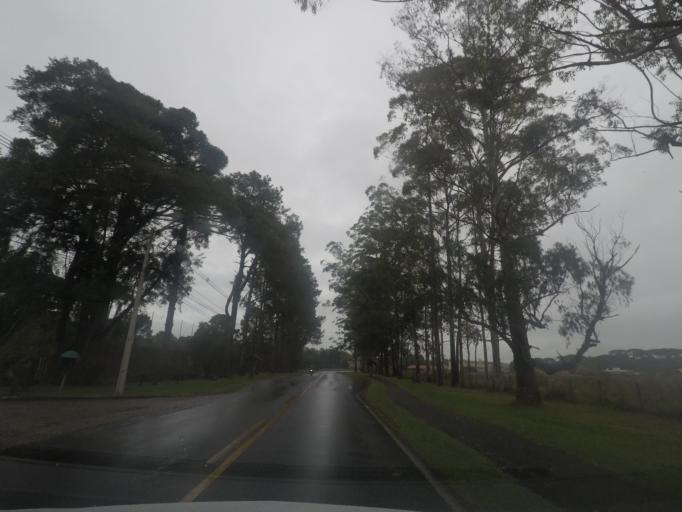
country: BR
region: Parana
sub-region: Quatro Barras
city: Quatro Barras
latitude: -25.3739
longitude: -49.0917
